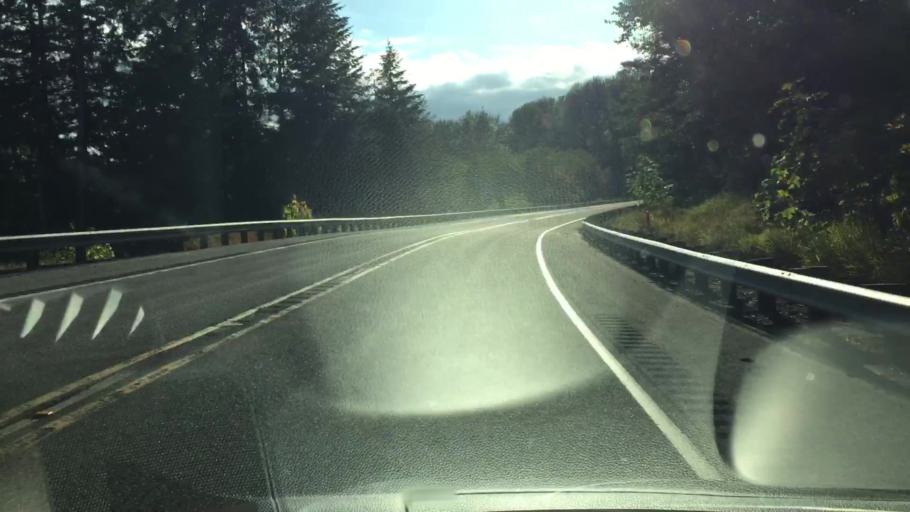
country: US
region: Washington
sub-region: Lewis County
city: Morton
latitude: 46.5095
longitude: -122.1827
